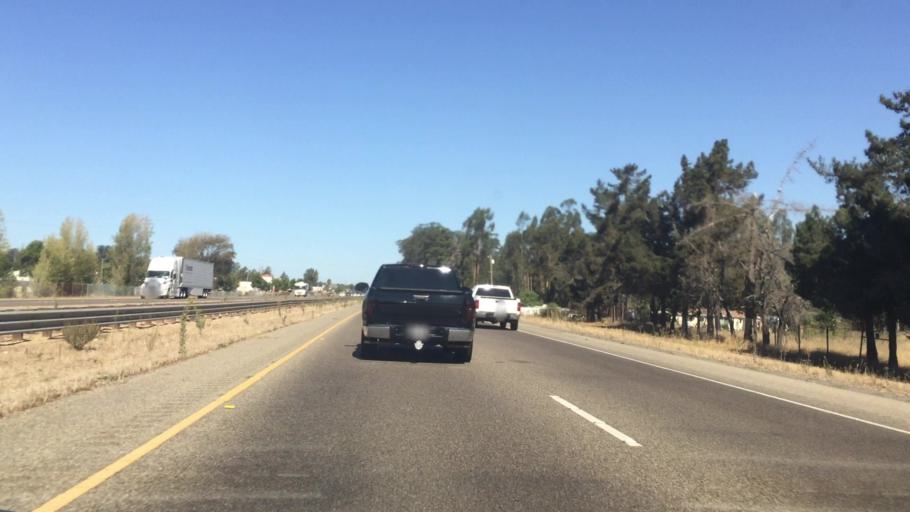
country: US
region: California
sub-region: San Luis Obispo County
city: Nipomo
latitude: 35.0227
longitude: -120.4692
